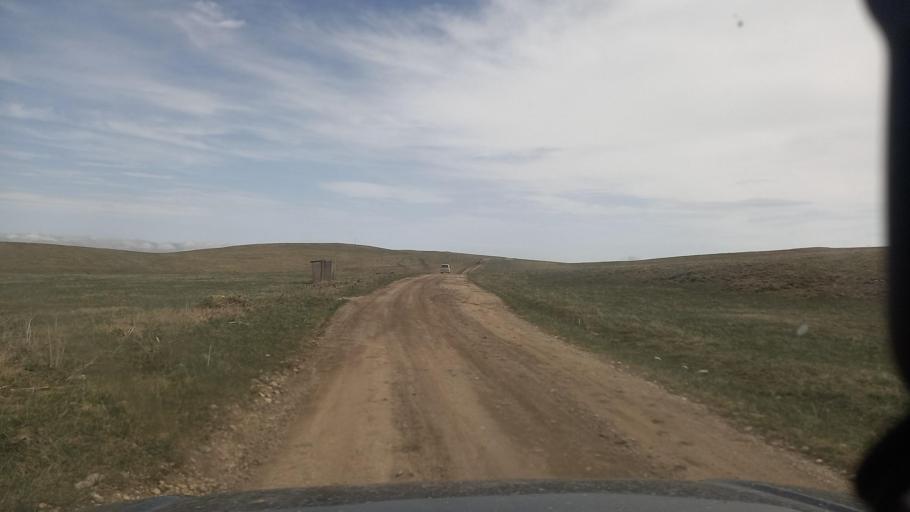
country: RU
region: Stavropol'skiy
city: Kislovodsk
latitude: 43.7538
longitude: 42.7509
